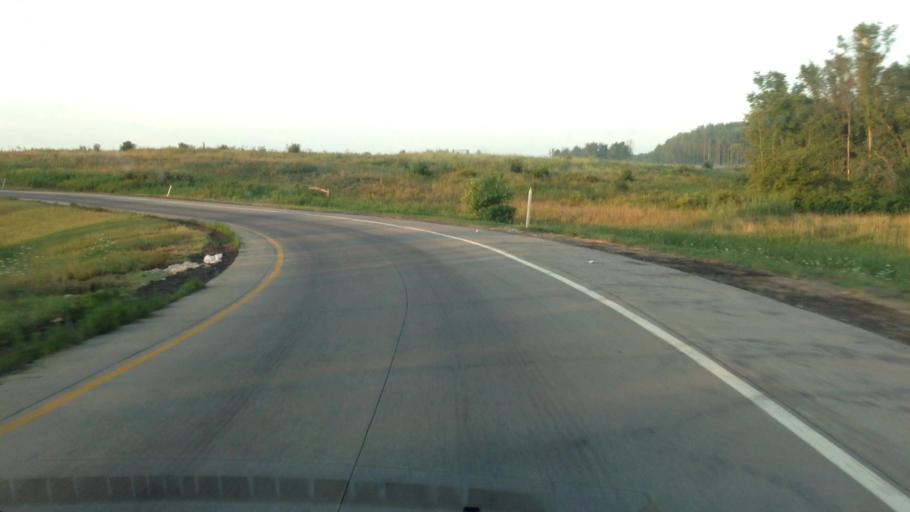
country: US
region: Ohio
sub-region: Summit County
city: Silver Lake
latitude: 41.2023
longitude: -81.4849
